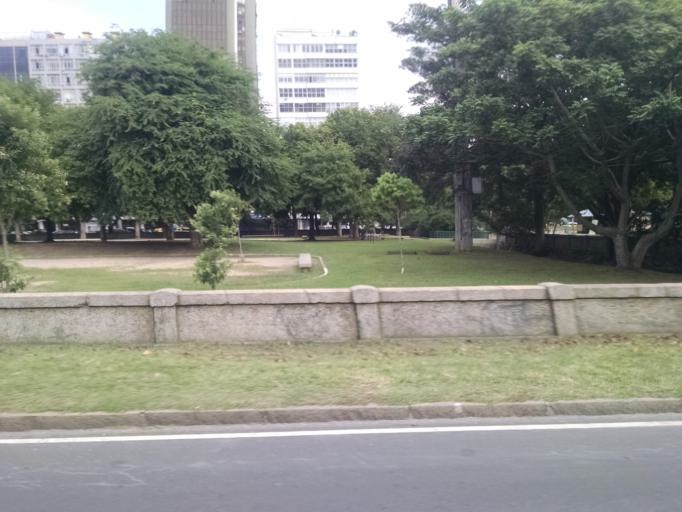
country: BR
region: Rio de Janeiro
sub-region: Rio De Janeiro
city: Rio de Janeiro
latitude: -22.9247
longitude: -43.1714
